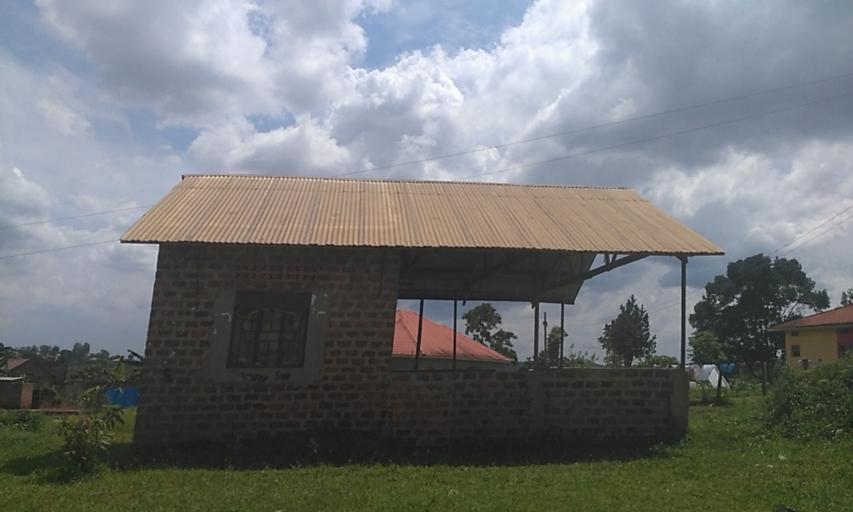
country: UG
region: Central Region
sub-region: Wakiso District
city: Wakiso
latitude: 0.3953
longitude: 32.4706
